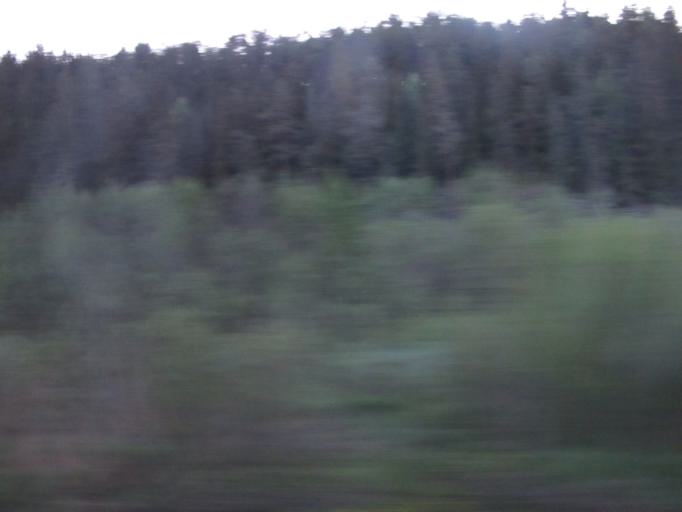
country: NO
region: Oppland
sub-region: Ringebu
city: Ringebu
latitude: 61.5349
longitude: 10.1079
